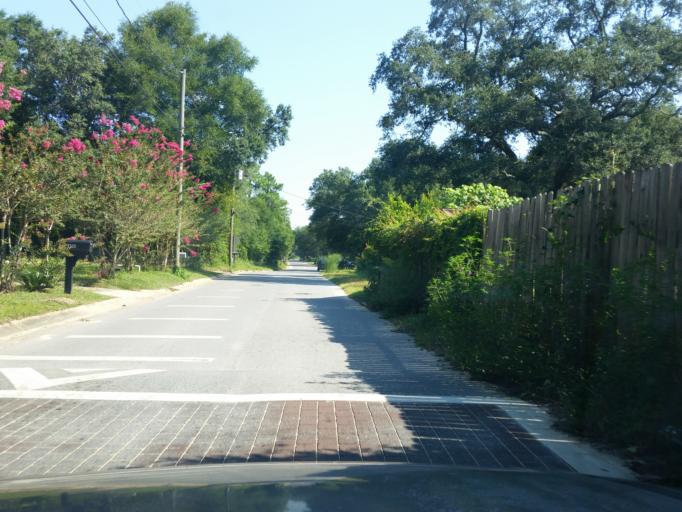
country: US
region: Florida
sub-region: Escambia County
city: Ferry Pass
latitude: 30.5112
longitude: -87.2044
